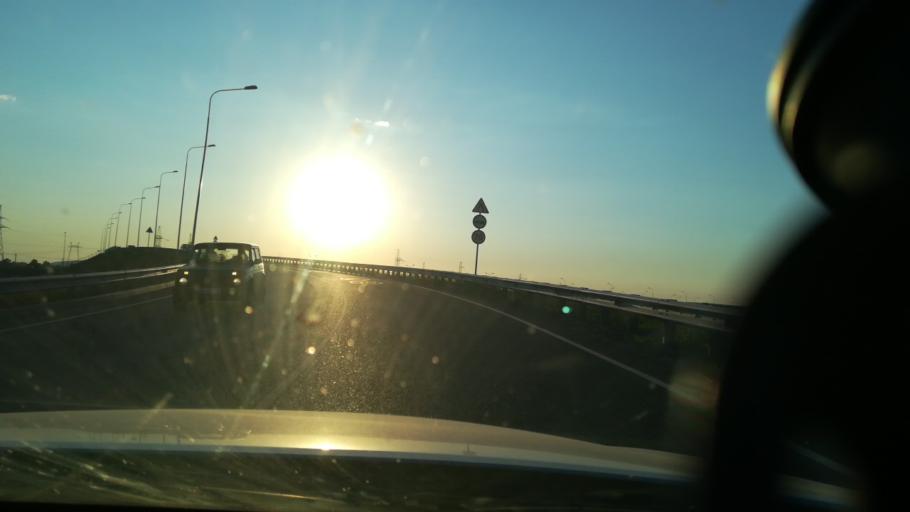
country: RU
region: Krasnodarskiy
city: Dzhiginka
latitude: 45.1365
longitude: 37.3198
